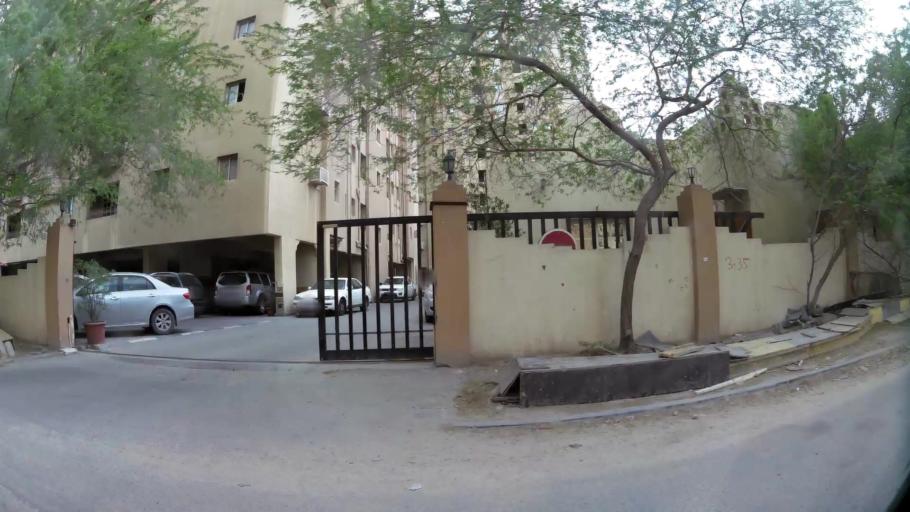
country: QA
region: Baladiyat ad Dawhah
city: Doha
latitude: 25.2822
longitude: 51.5201
